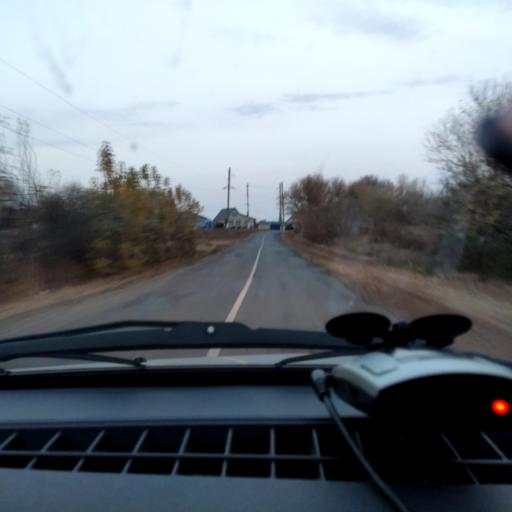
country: RU
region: Voronezj
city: Uryv-Pokrovka
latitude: 51.2277
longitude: 38.9140
